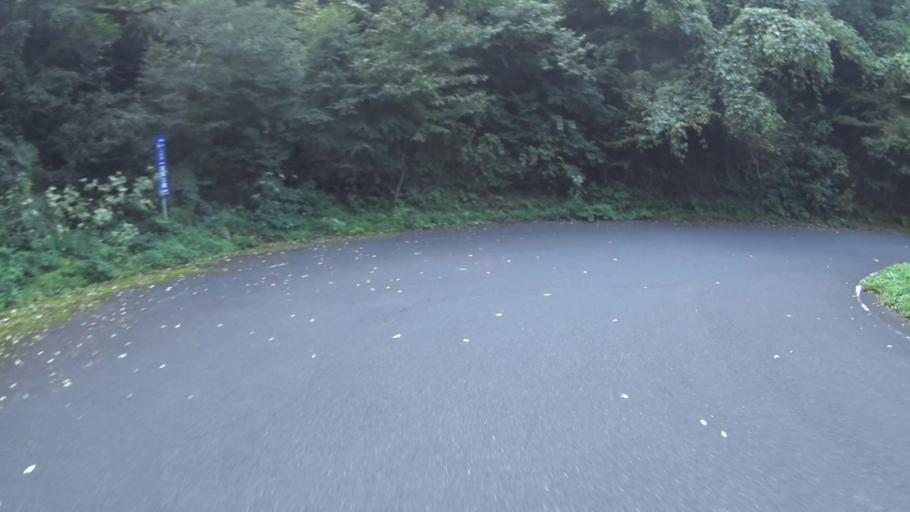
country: JP
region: Kyoto
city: Miyazu
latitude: 35.5674
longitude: 135.1382
